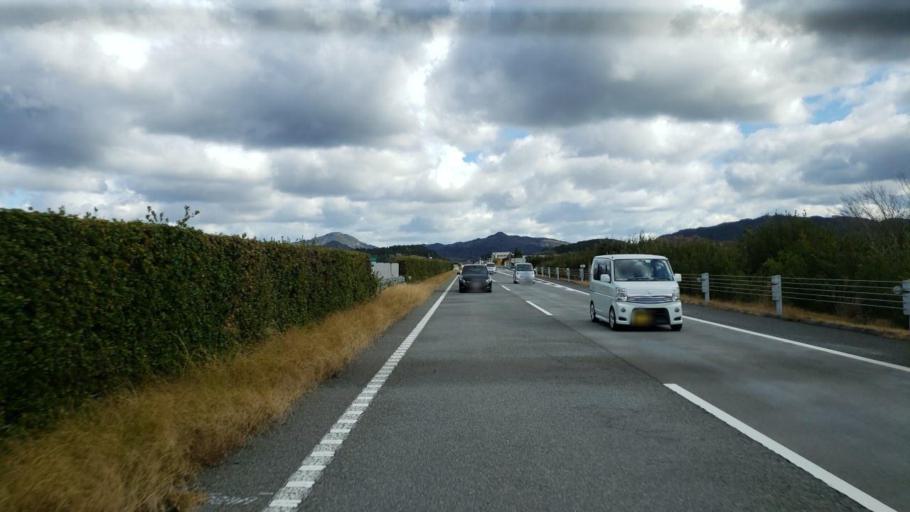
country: JP
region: Hyogo
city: Fukura
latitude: 34.3173
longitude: 134.7670
